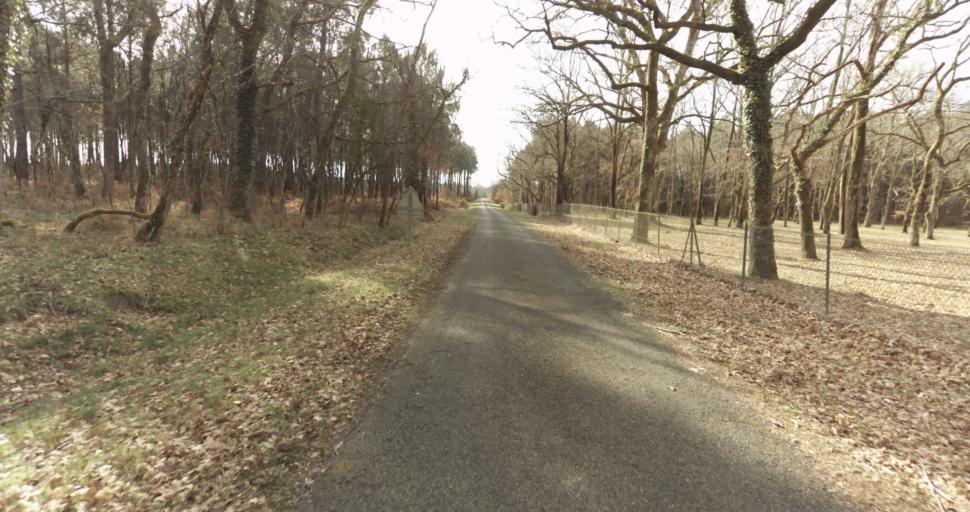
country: FR
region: Aquitaine
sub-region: Departement des Landes
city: Roquefort
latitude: 44.1180
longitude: -0.3014
